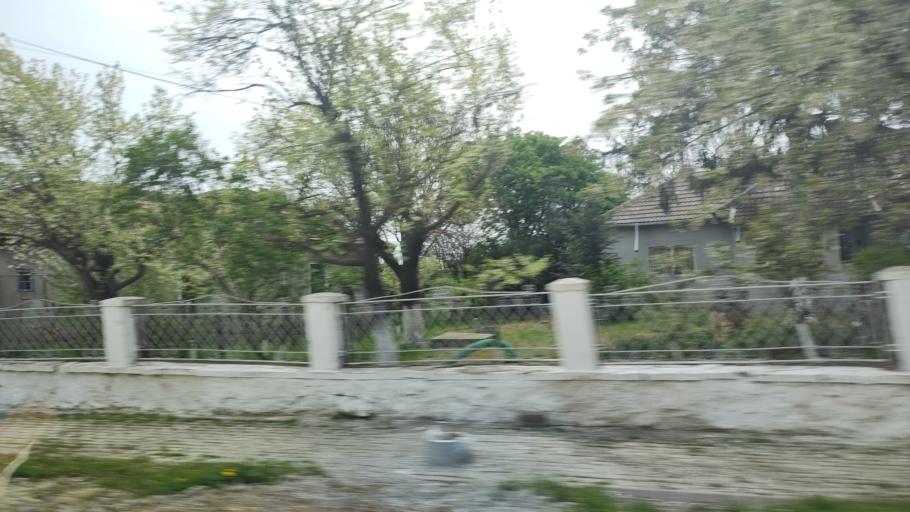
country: RO
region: Constanta
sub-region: Comuna Ciocarlia
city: Ciocarlia
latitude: 44.1037
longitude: 28.2833
